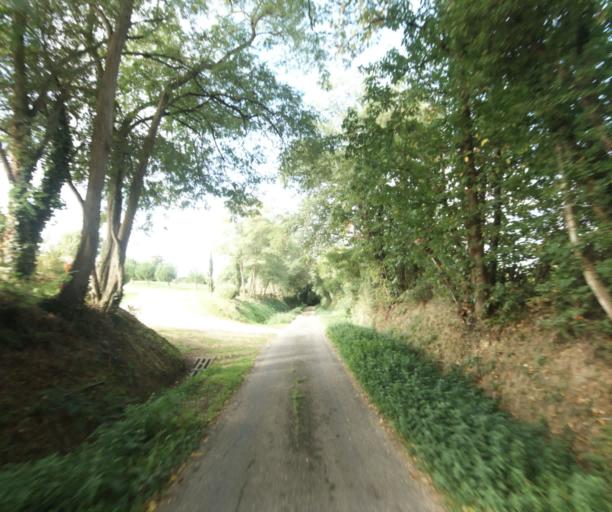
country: FR
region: Midi-Pyrenees
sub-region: Departement du Gers
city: Cazaubon
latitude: 43.8624
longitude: -0.0675
